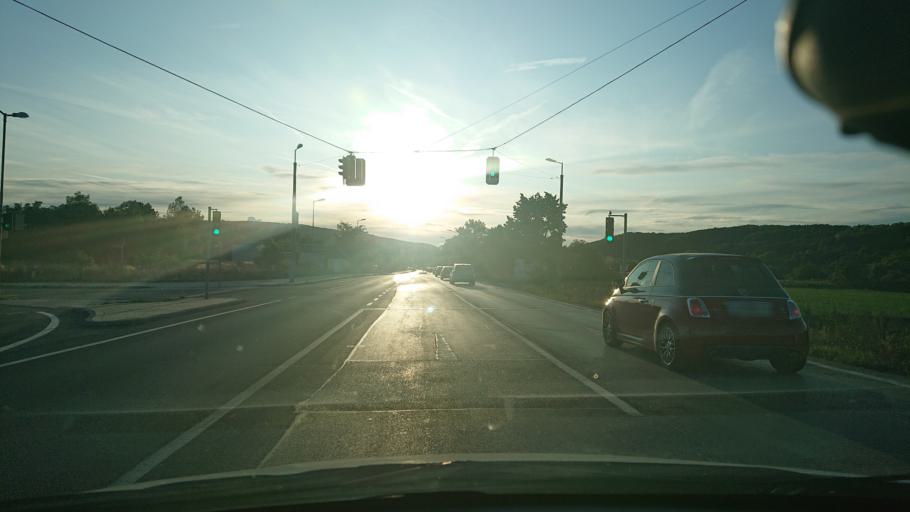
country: AT
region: Lower Austria
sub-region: Politischer Bezirk Baden
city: Hirtenberg
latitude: 47.9316
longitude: 16.1977
